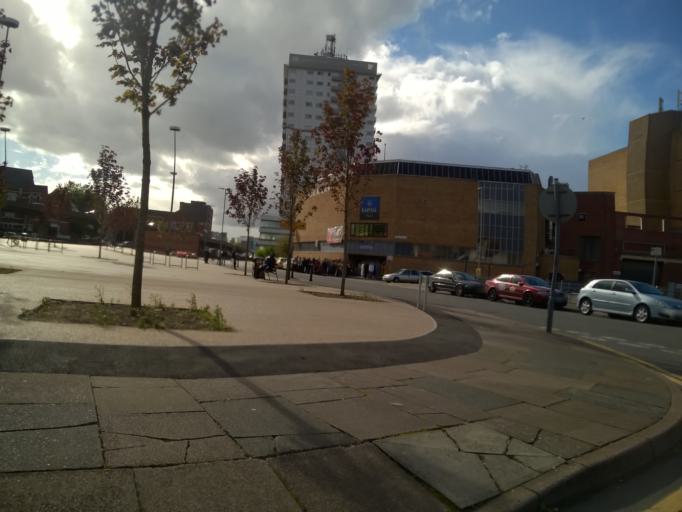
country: GB
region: England
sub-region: City of Leicester
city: Leicester
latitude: 52.6422
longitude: -1.1292
